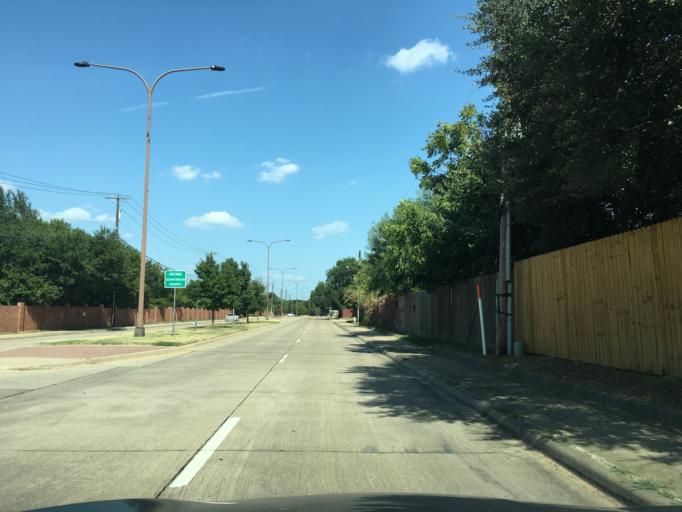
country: US
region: Texas
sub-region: Tarrant County
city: Dalworthington Gardens
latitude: 32.6801
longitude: -97.1645
